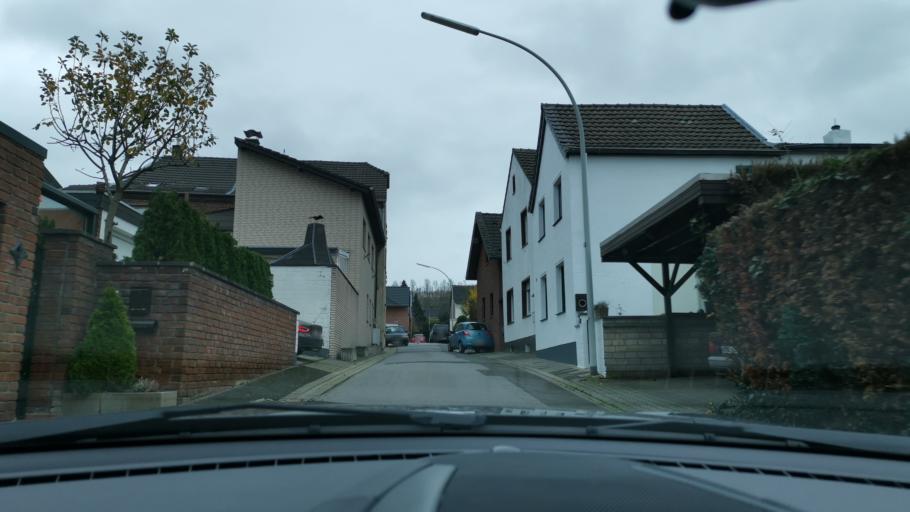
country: DE
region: North Rhine-Westphalia
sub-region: Regierungsbezirk Dusseldorf
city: Grevenbroich
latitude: 51.0703
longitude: 6.5882
